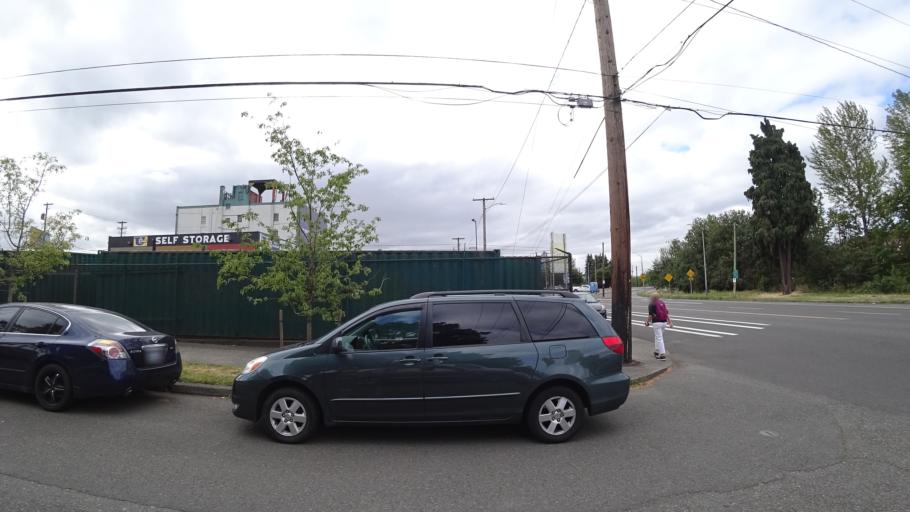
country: US
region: Oregon
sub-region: Multnomah County
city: Portland
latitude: 45.5344
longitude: -122.6719
